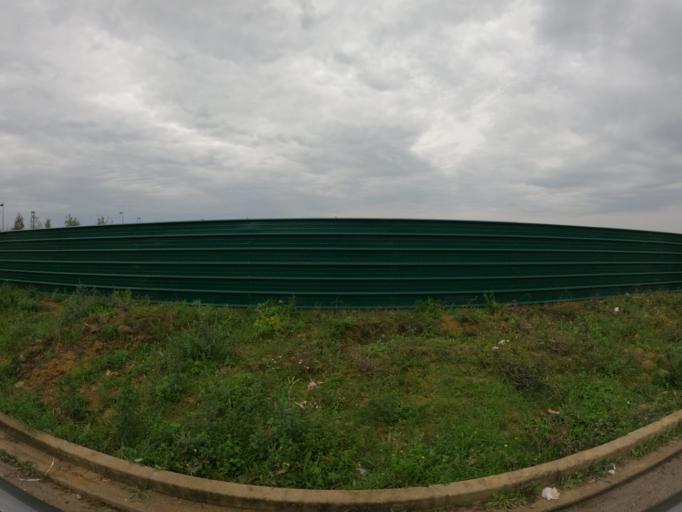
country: FR
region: Ile-de-France
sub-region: Departement de Seine-et-Marne
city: Serris
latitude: 48.8375
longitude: 2.8009
